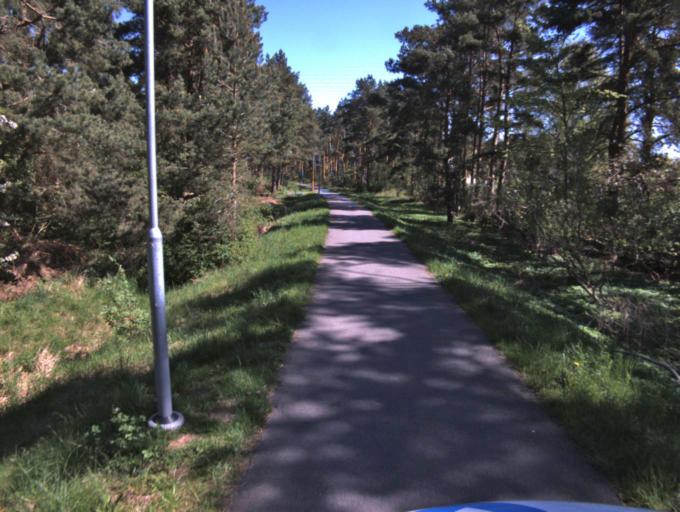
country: SE
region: Skane
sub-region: Kristianstads Kommun
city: Degeberga
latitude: 55.9004
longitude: 14.1005
